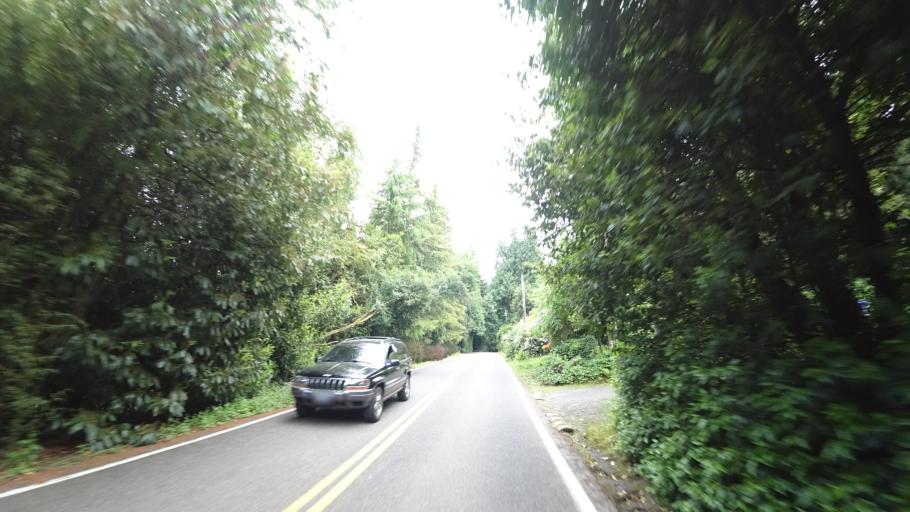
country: US
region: Oregon
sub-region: Clackamas County
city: Milwaukie
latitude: 45.4458
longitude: -122.6600
